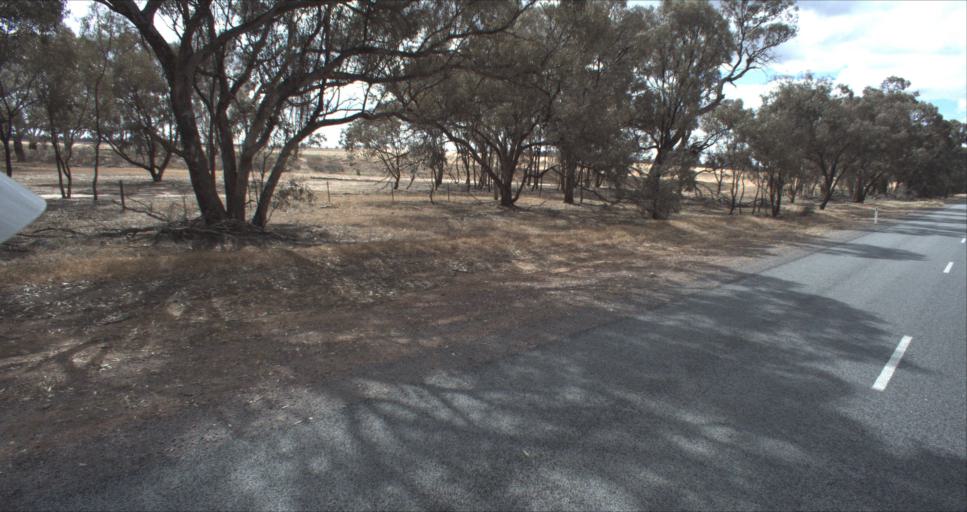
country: AU
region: New South Wales
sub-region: Leeton
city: Leeton
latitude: -34.6649
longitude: 146.3486
